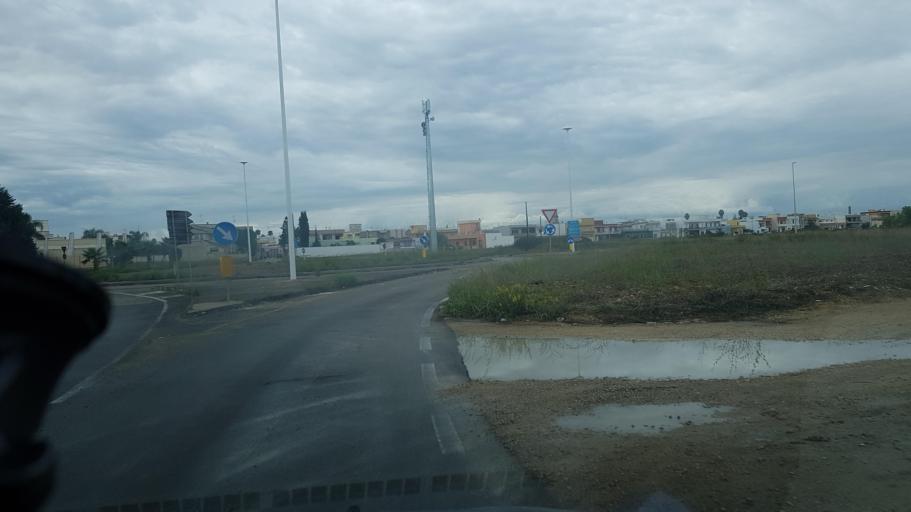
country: IT
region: Apulia
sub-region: Provincia di Lecce
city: Salice Salentino
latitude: 40.3804
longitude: 17.9707
